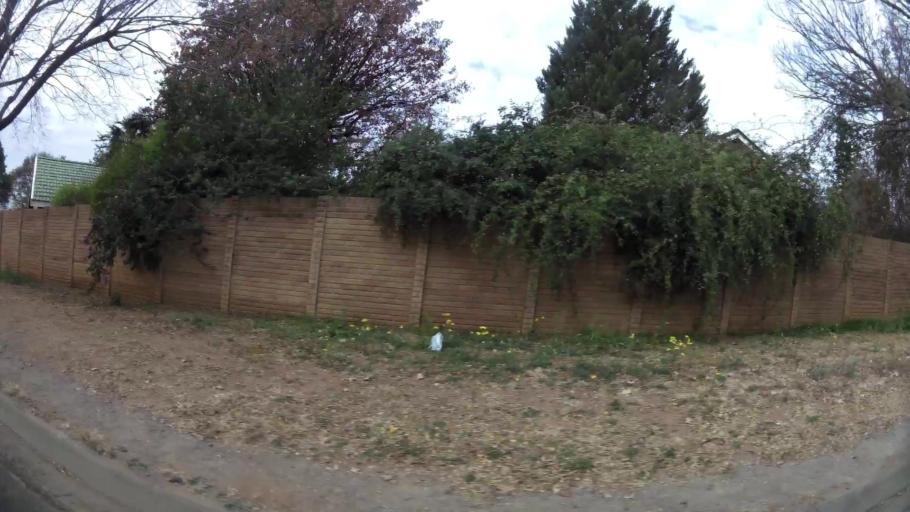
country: ZA
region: Orange Free State
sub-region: Mangaung Metropolitan Municipality
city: Bloemfontein
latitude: -29.0976
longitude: 26.2126
